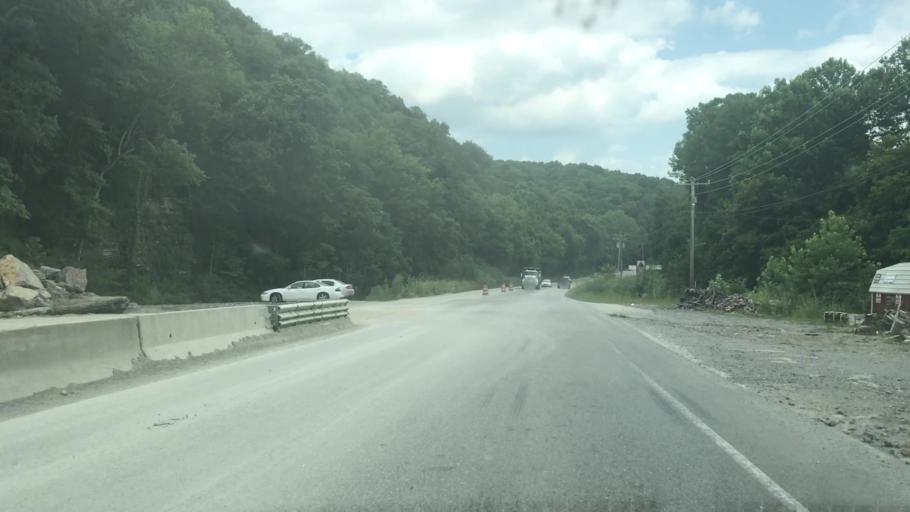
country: US
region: Tennessee
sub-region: Smith County
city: Carthage
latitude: 36.2705
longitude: -85.9764
